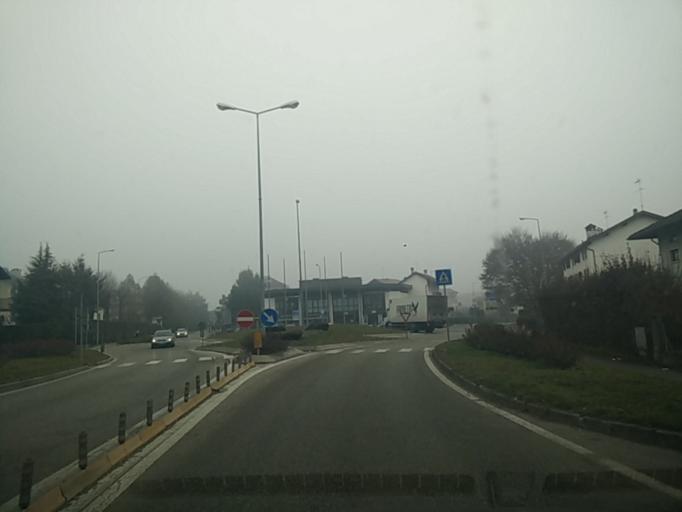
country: IT
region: Veneto
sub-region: Provincia di Belluno
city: Feltre
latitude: 46.0194
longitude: 11.8947
